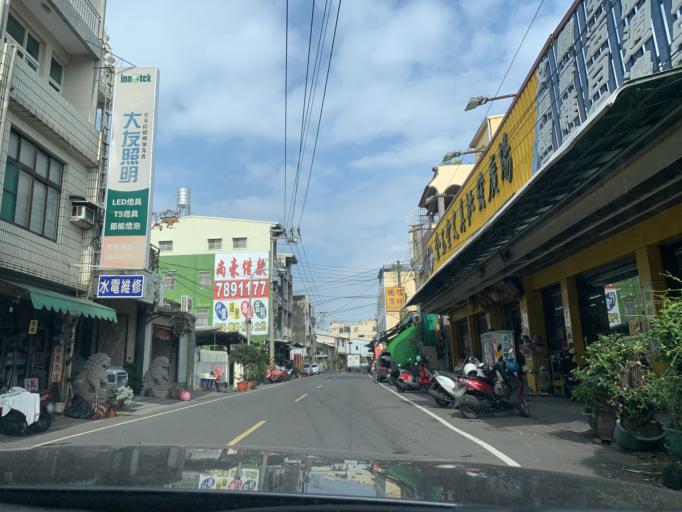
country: TW
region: Taiwan
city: Fengshan
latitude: 22.4672
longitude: 120.4473
